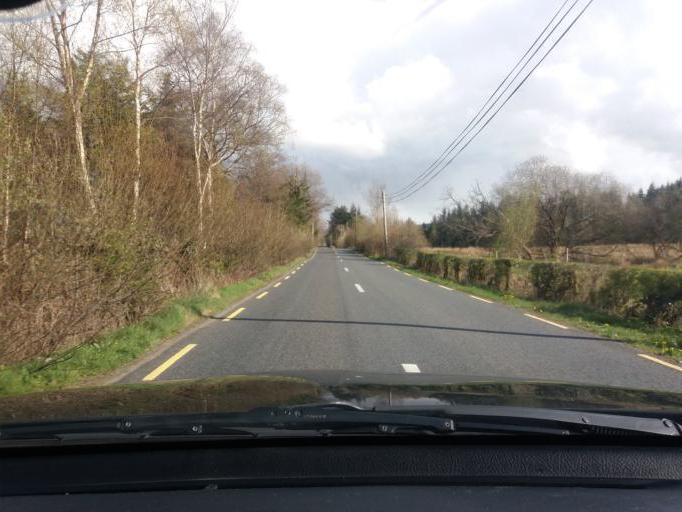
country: IE
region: Connaught
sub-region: County Leitrim
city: Manorhamilton
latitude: 54.3396
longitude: -8.2248
